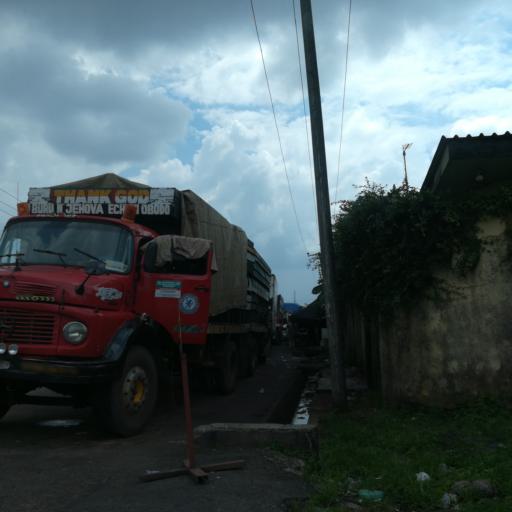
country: NG
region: Rivers
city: Port Harcourt
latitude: 4.8118
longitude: 7.0376
